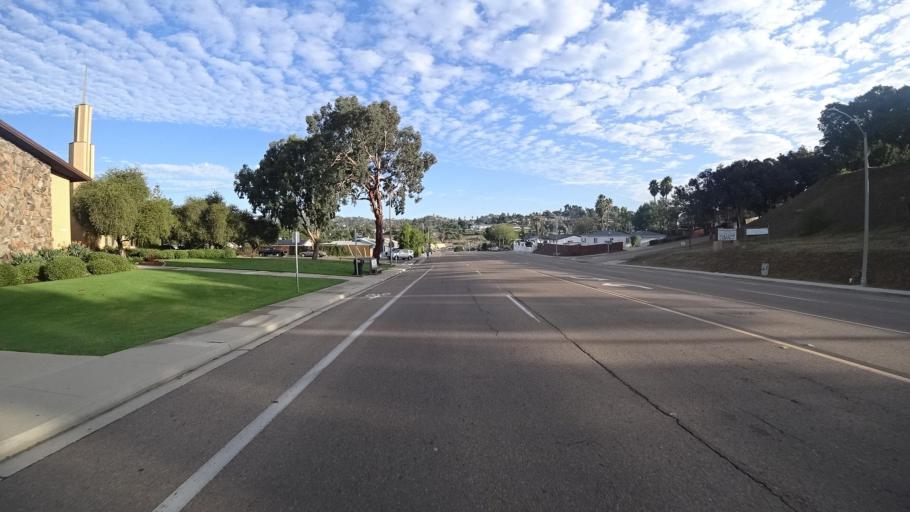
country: US
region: California
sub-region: San Diego County
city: Casa de Oro-Mount Helix
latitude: 32.7399
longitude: -116.9726
